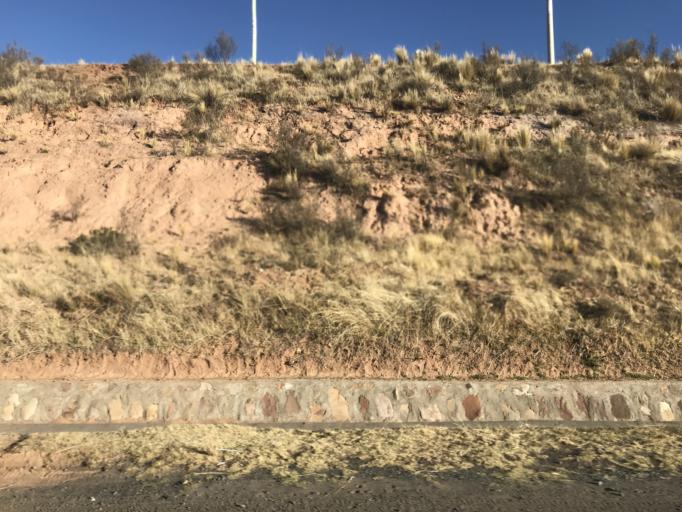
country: BO
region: La Paz
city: Tiahuanaco
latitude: -16.5663
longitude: -68.6454
